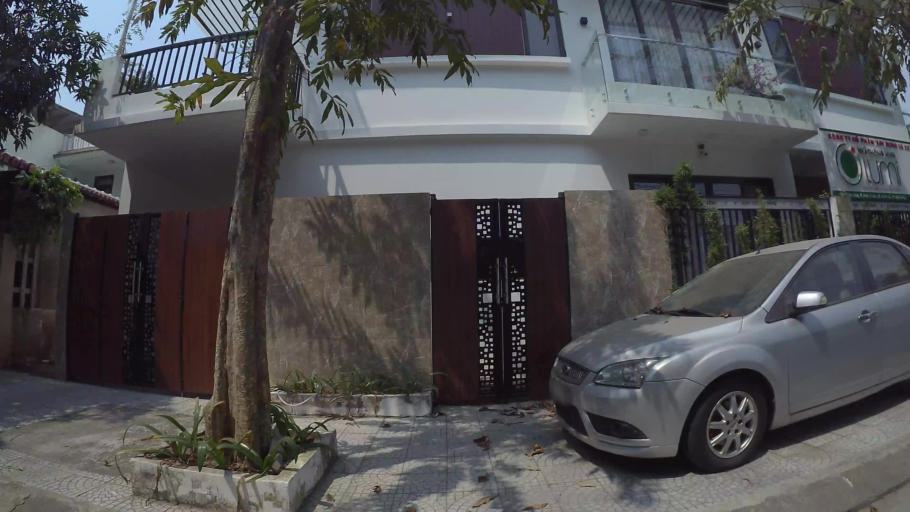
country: VN
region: Da Nang
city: Cam Le
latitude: 16.0033
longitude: 108.2114
